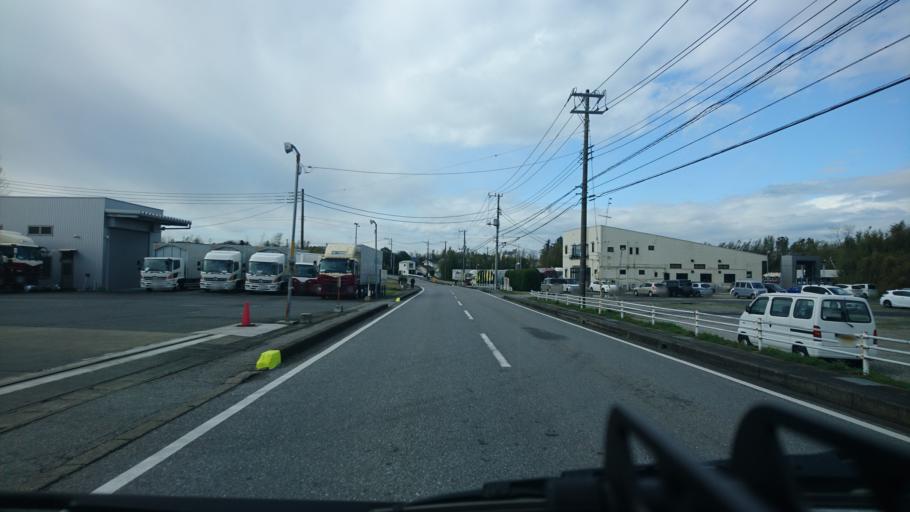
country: JP
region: Chiba
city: Kimitsu
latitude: 35.3105
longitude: 139.9613
